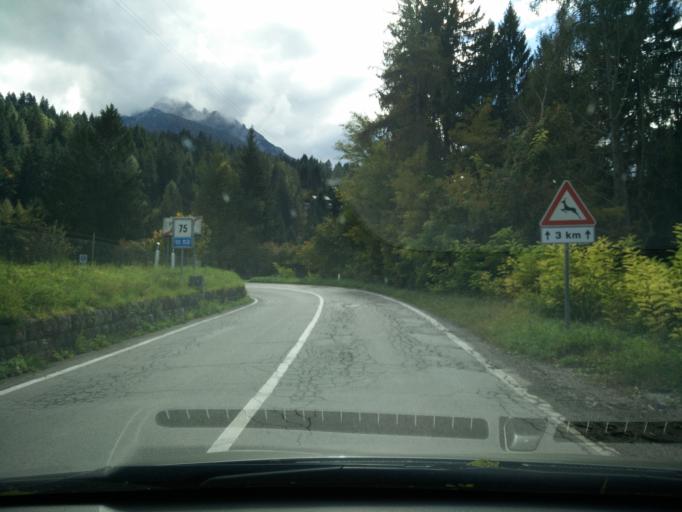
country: IT
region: Veneto
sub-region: Provincia di Belluno
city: Lorenzago di Cadore
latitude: 46.4883
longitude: 12.4639
